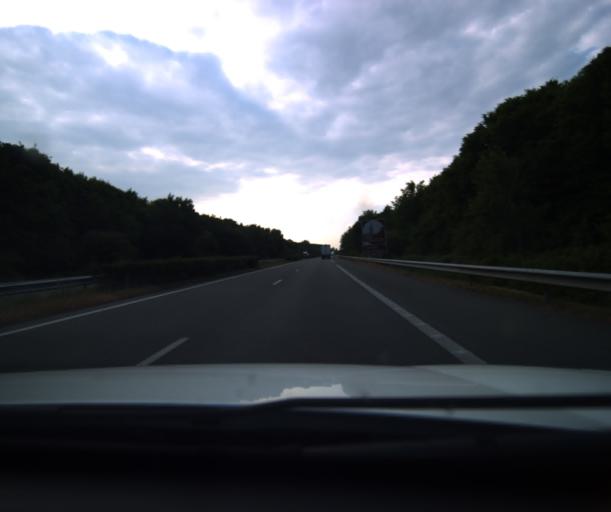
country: FR
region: Midi-Pyrenees
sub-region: Departement du Tarn-et-Garonne
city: Montech
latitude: 43.9912
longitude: 1.2349
